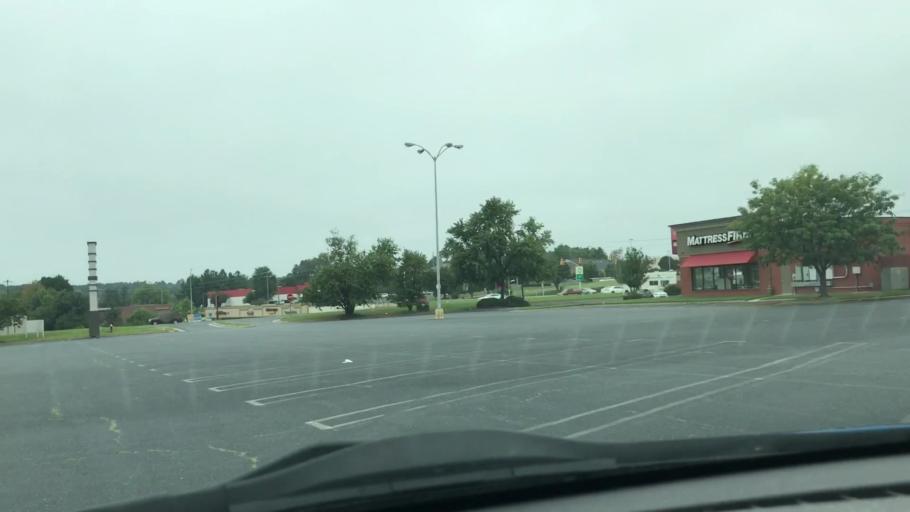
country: US
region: North Carolina
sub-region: Randolph County
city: Asheboro
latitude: 35.6969
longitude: -79.7872
